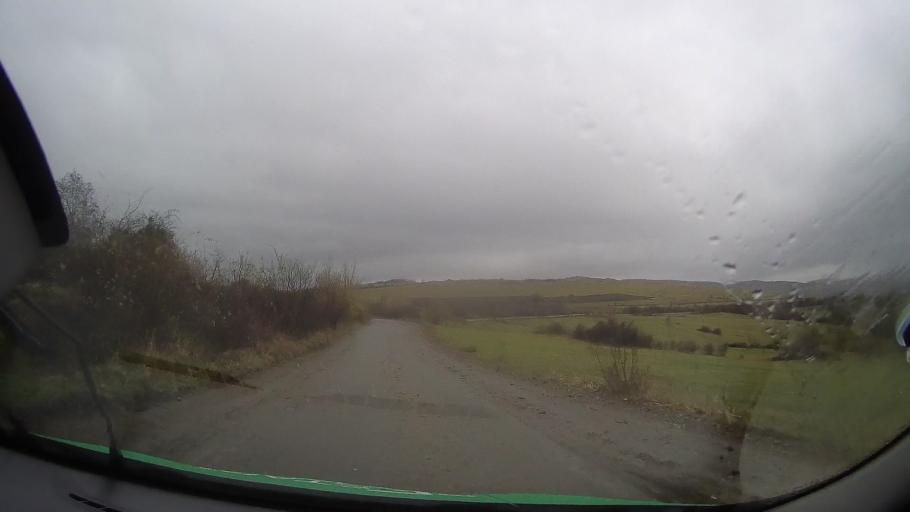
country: RO
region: Mures
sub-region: Comuna Vatava
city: Vatava
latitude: 46.9515
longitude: 24.7345
